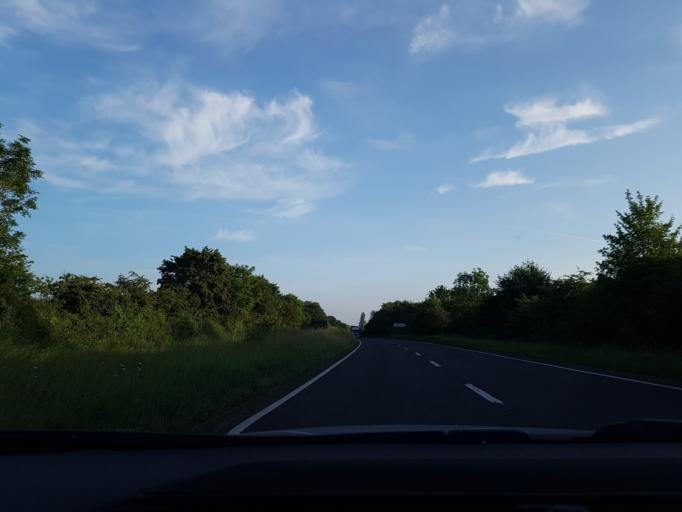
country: GB
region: England
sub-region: Northamptonshire
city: Deanshanger
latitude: 52.0276
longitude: -0.9104
